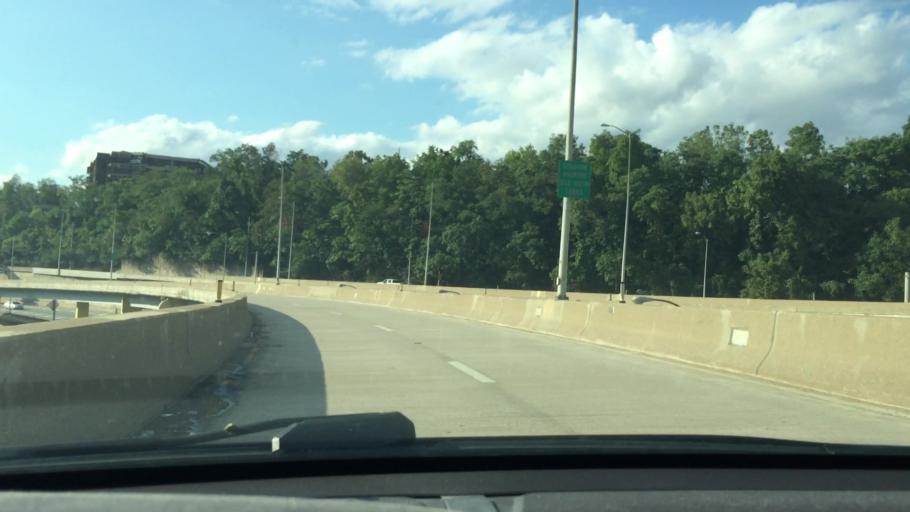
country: US
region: Pennsylvania
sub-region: Allegheny County
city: Pittsburgh
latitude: 40.4477
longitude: -80.0113
